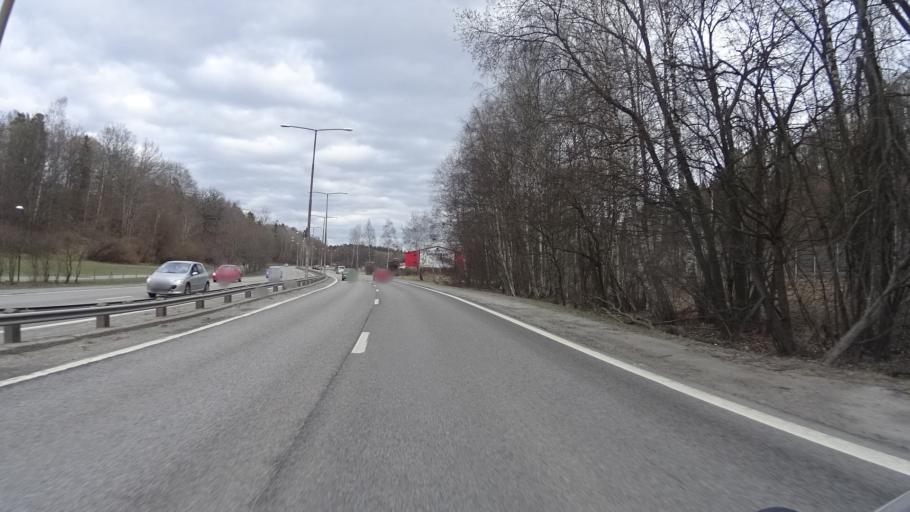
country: SE
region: Stockholm
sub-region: Stockholms Kommun
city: Arsta
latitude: 59.2634
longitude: 18.0273
